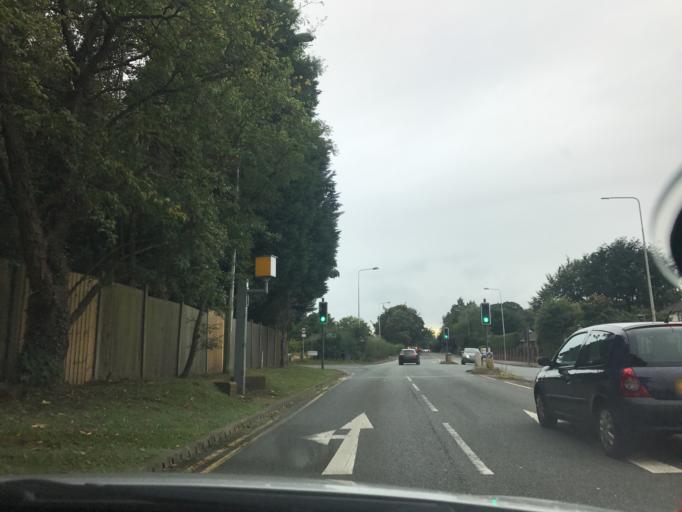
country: GB
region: England
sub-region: Cheshire West and Chester
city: Cuddington
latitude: 53.2310
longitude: -2.5936
